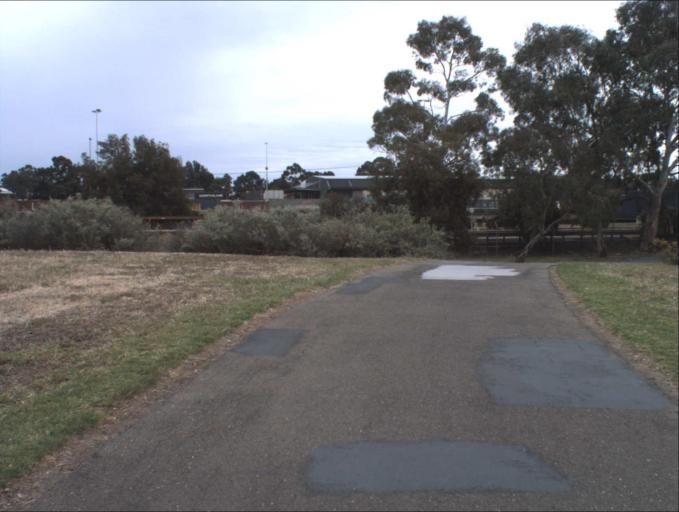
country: AU
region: South Australia
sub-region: Port Adelaide Enfield
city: Blair Athol
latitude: -34.8608
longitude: 138.5791
